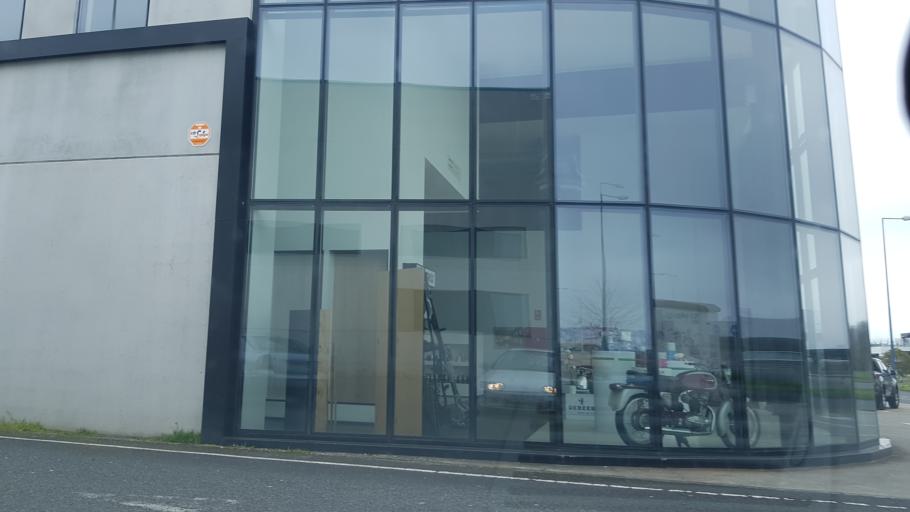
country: ES
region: Galicia
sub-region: Provincia de Lugo
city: Lugo
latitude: 43.0391
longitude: -7.5539
